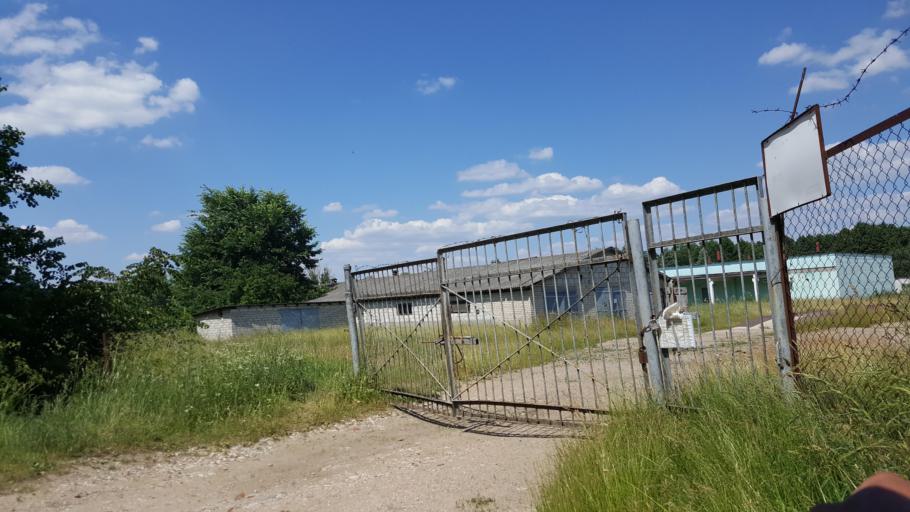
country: BY
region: Brest
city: Kamyanyets
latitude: 52.4107
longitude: 23.8265
